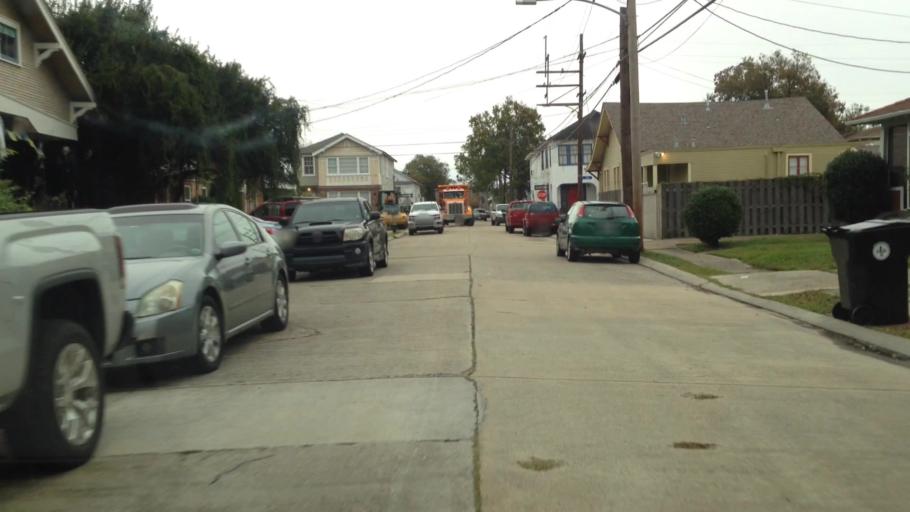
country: US
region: Louisiana
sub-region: Orleans Parish
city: New Orleans
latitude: 29.9521
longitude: -90.1054
